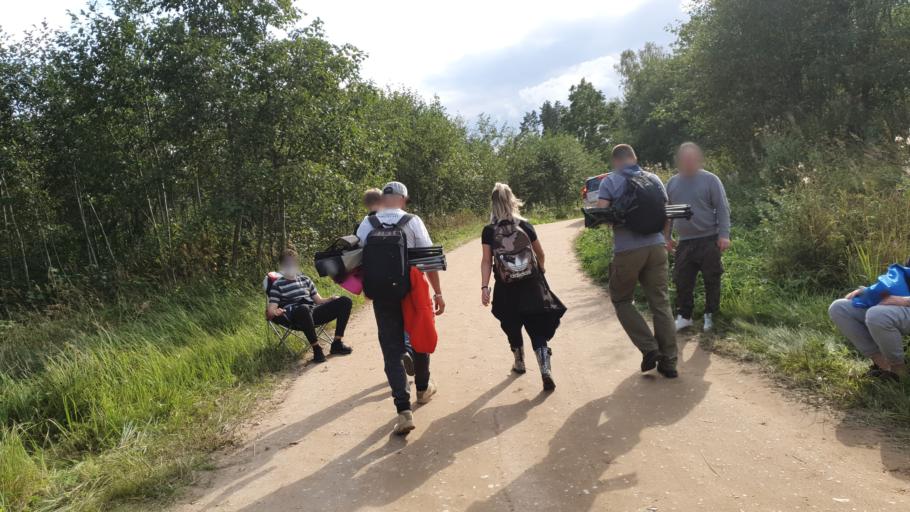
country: EE
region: Tartu
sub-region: UElenurme vald
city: Ulenurme
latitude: 58.1297
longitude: 26.7460
